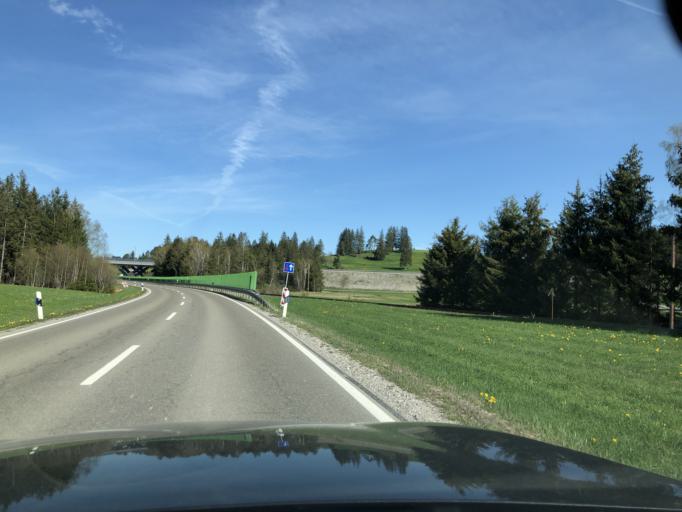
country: DE
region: Bavaria
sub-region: Swabia
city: Eisenberg
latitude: 47.6264
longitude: 10.6052
